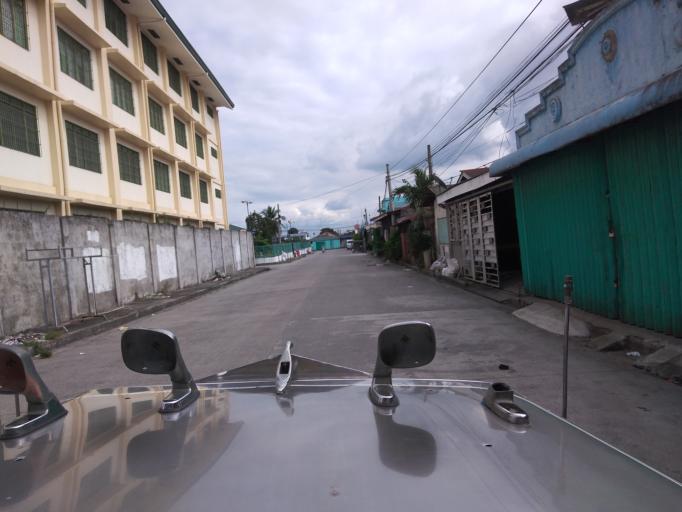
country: PH
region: Central Luzon
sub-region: Province of Pampanga
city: Pandacaqui
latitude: 15.1771
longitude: 120.6446
